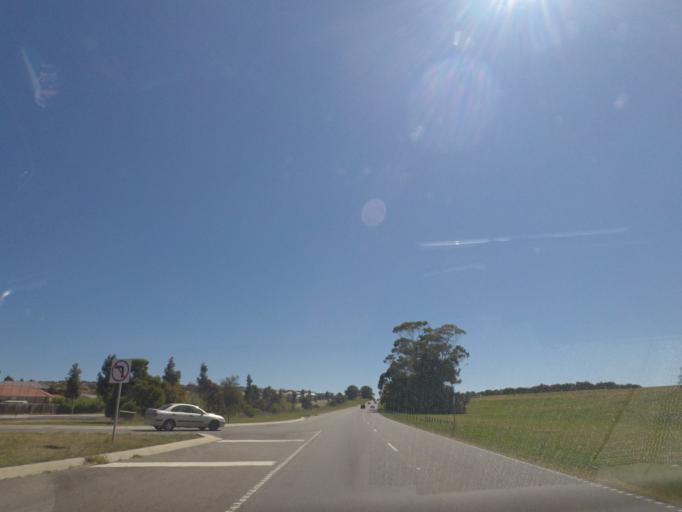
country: AU
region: Victoria
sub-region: Hume
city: Craigieburn
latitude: -37.5767
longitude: 144.9393
